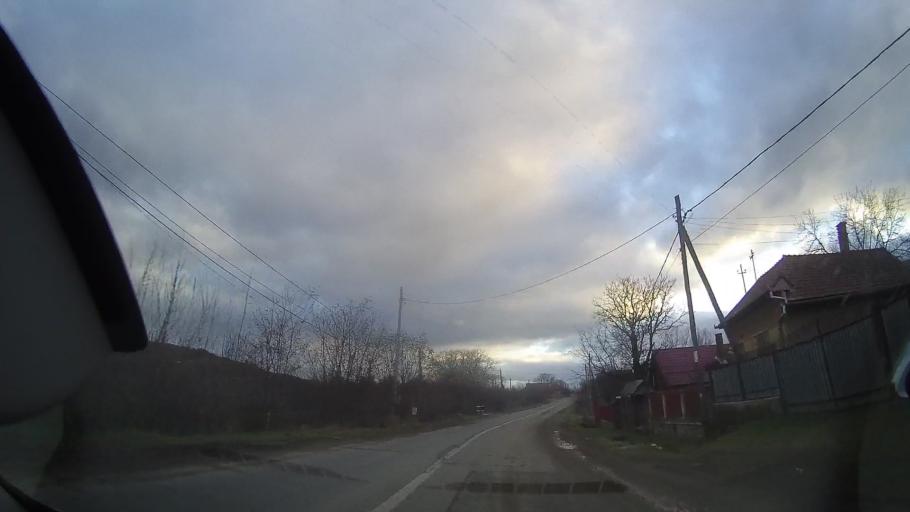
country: RO
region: Cluj
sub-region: Comuna Sancraiu
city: Sancraiu
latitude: 46.8071
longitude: 22.9940
